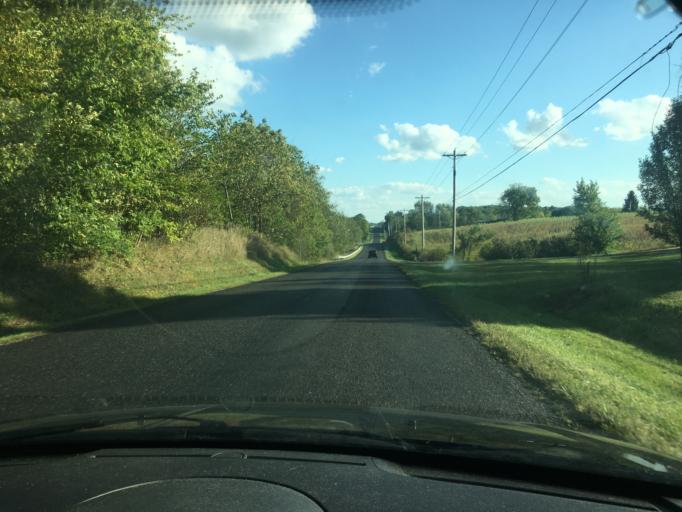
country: US
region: Ohio
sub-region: Logan County
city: Bellefontaine
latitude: 40.3080
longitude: -83.7353
